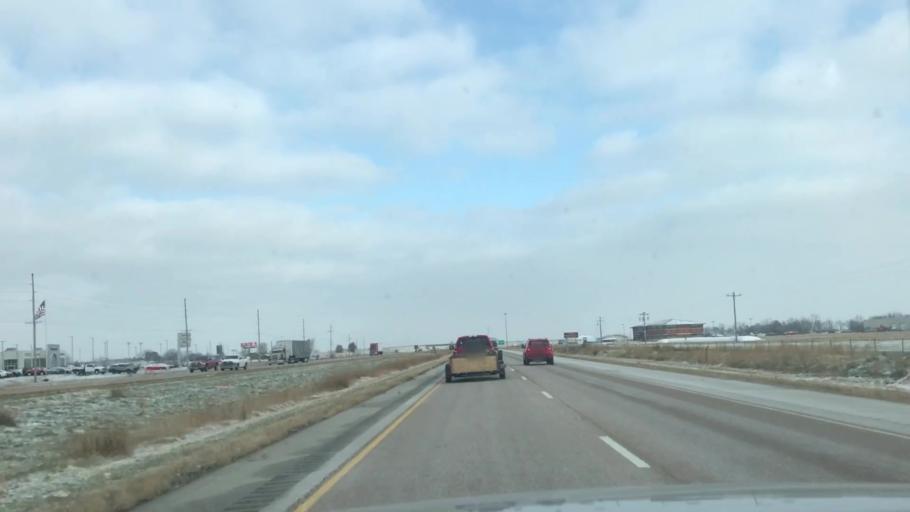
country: US
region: Illinois
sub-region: Macoupin County
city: Staunton
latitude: 39.0108
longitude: -89.7495
